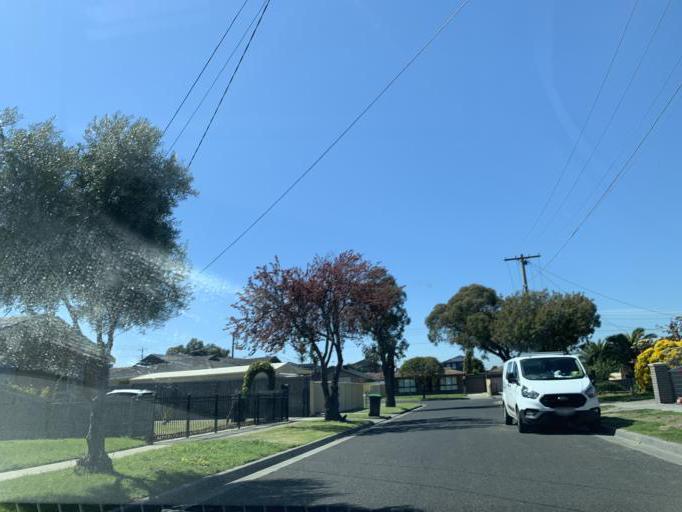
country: AU
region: Victoria
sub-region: Greater Dandenong
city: Dandenong
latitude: -37.9989
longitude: 145.2034
